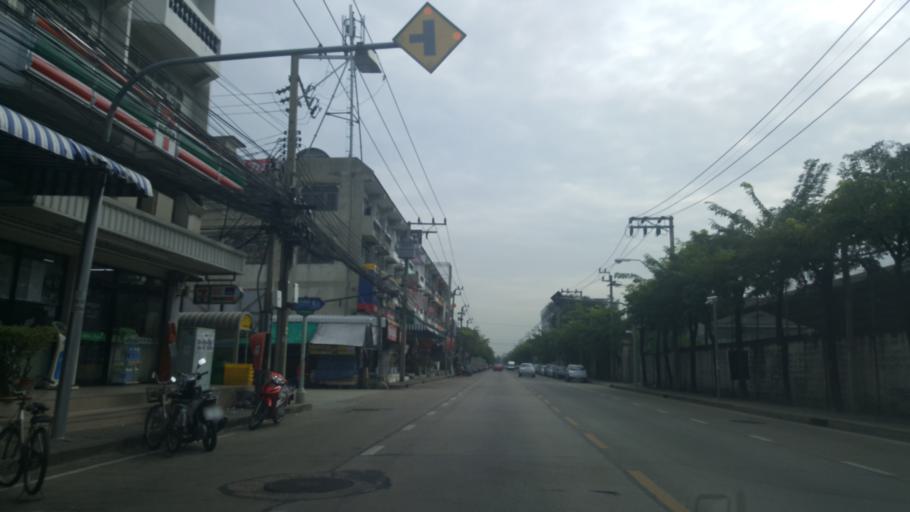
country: TH
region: Bangkok
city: Nong Khaem
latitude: 13.6907
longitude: 100.3729
